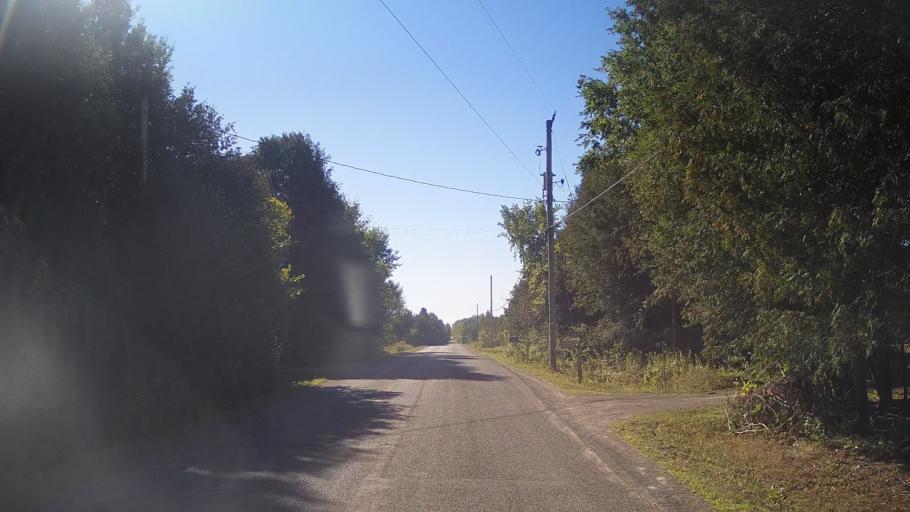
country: CA
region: Ontario
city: Prescott
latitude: 44.9905
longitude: -75.5877
